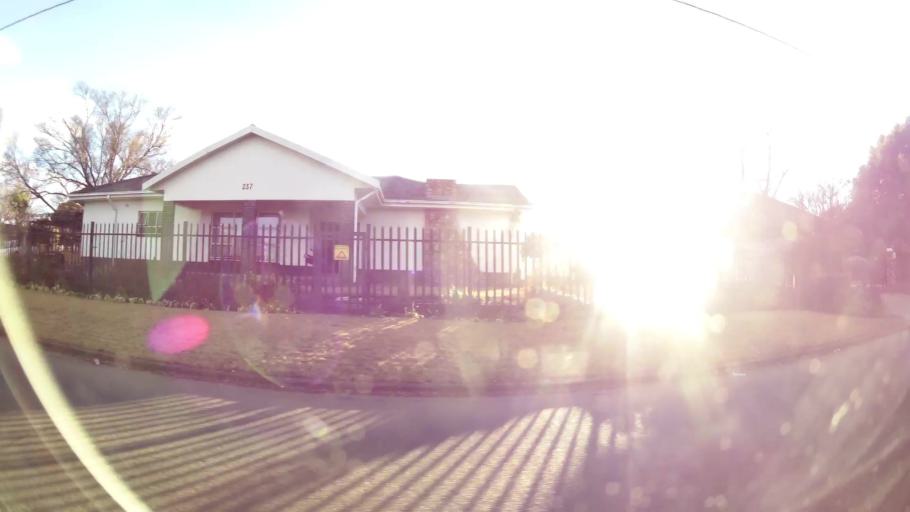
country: ZA
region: North-West
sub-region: Dr Kenneth Kaunda District Municipality
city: Potchefstroom
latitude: -26.7309
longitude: 27.0997
